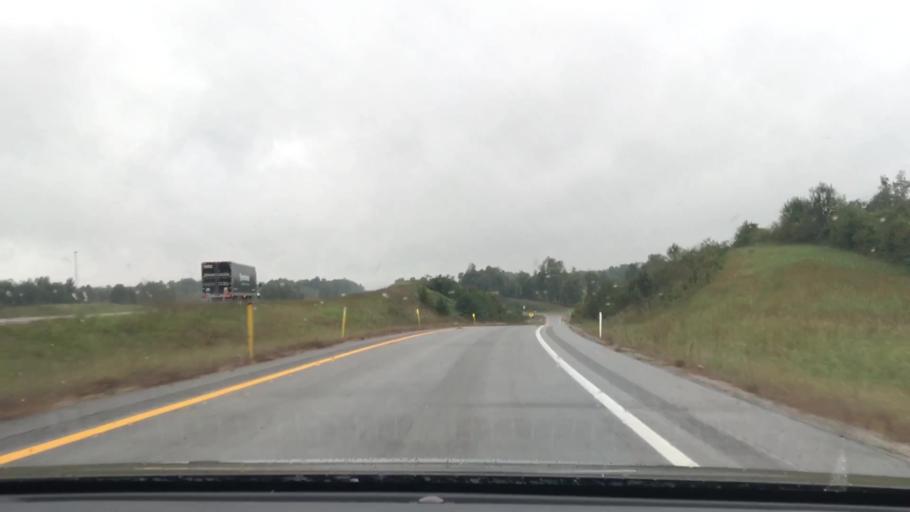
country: US
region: Kentucky
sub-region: Webster County
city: Sebree
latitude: 37.4861
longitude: -87.4753
